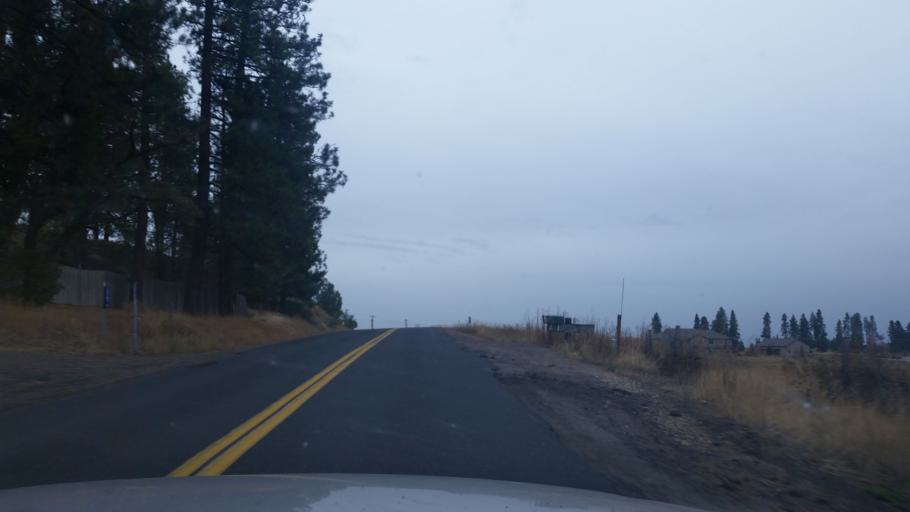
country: US
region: Washington
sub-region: Spokane County
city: Cheney
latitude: 47.5335
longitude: -117.5515
